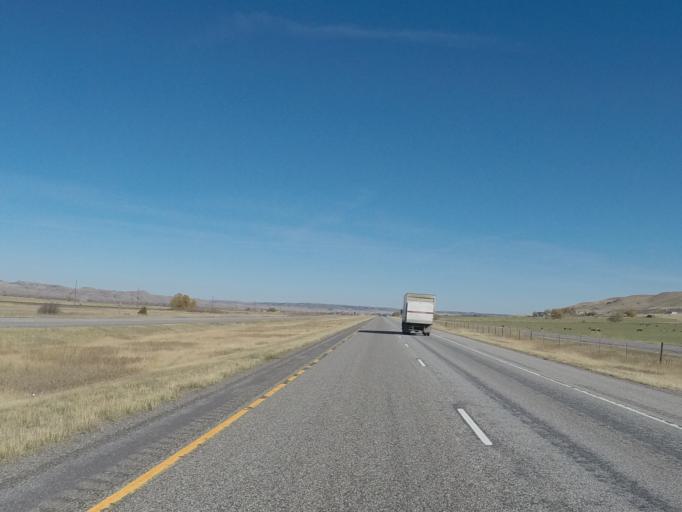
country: US
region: Montana
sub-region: Sweet Grass County
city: Big Timber
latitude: 45.8107
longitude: -110.0083
